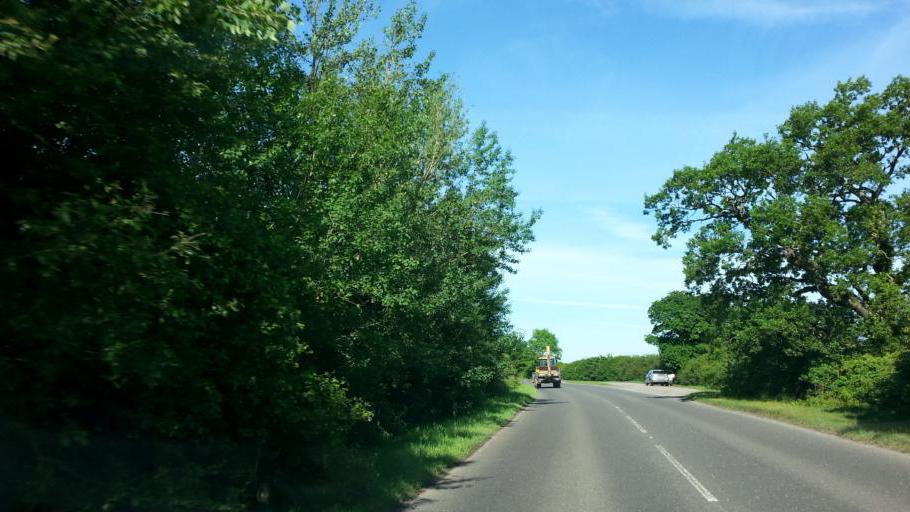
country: GB
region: England
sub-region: Nottinghamshire
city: Farnsfield
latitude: 53.0621
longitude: -1.0283
